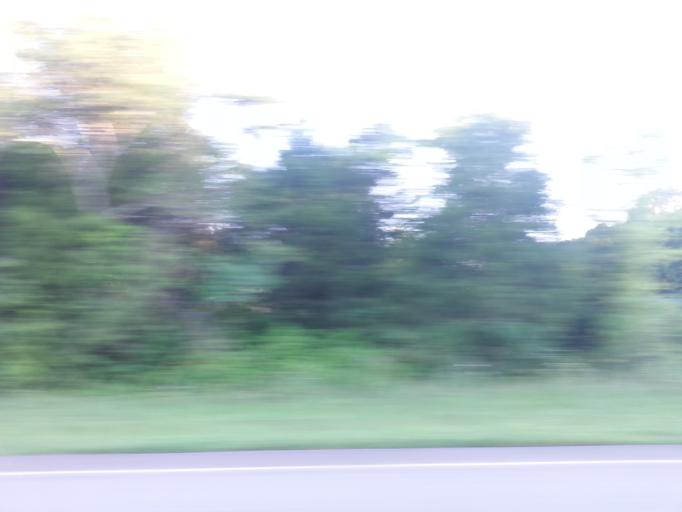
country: US
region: Tennessee
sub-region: Loudon County
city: Greenback
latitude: 35.6345
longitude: -84.2118
